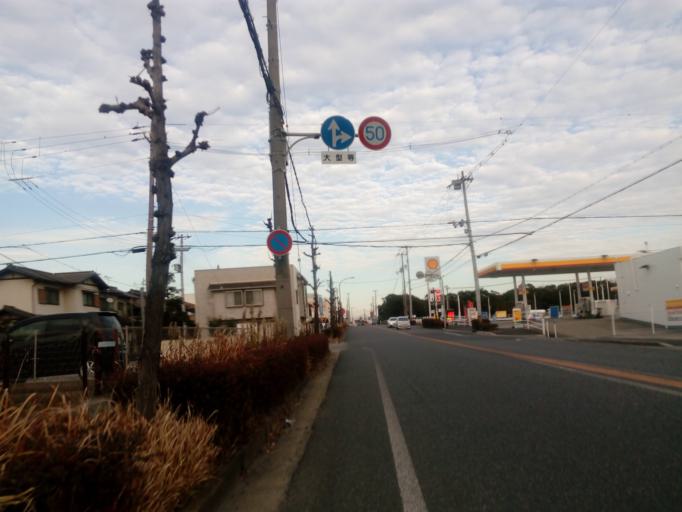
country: JP
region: Hyogo
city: Himeji
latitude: 34.7943
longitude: 134.6178
